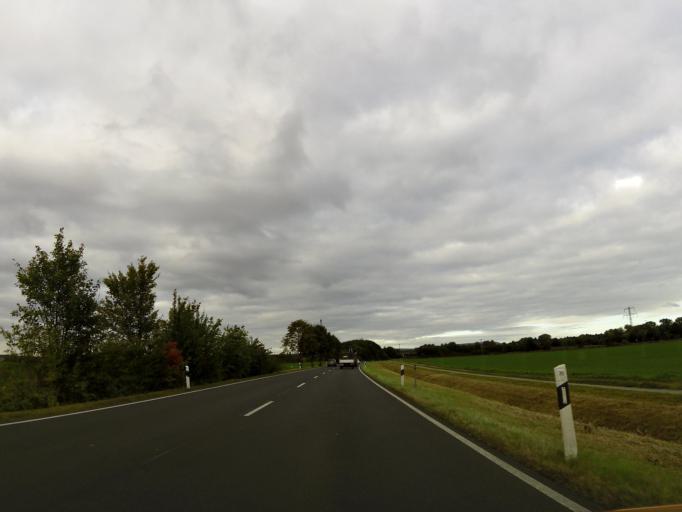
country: DE
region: Lower Saxony
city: Einbeck
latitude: 51.8045
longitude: 9.8595
